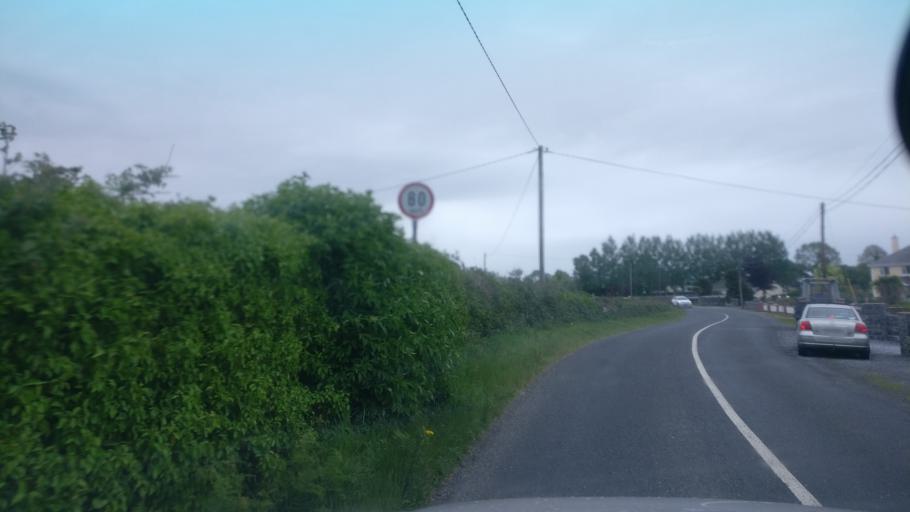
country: IE
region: Connaught
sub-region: County Galway
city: Gort
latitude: 53.0635
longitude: -8.7666
